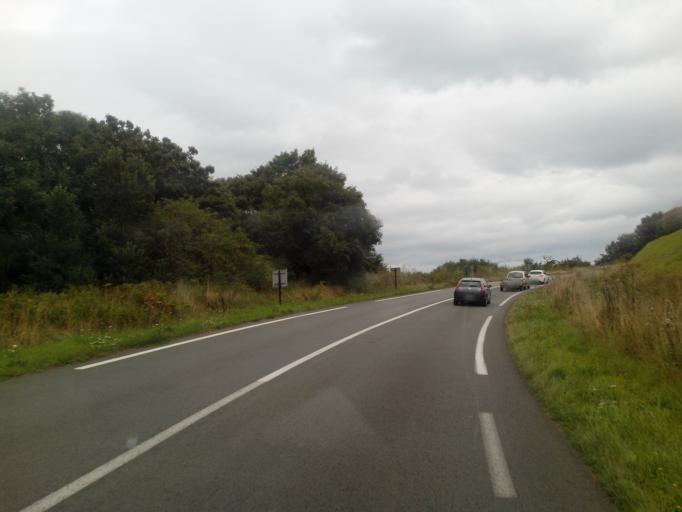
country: FR
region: Brittany
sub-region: Departement des Cotes-d'Armor
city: Etables-sur-Mer
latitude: 48.6352
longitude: -2.8276
